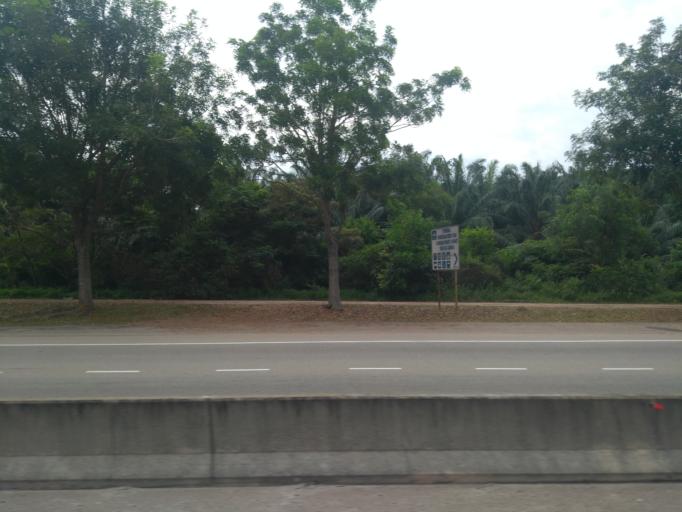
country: MY
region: Melaka
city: Kampung Ayer Keroh
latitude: 2.2865
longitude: 102.2676
